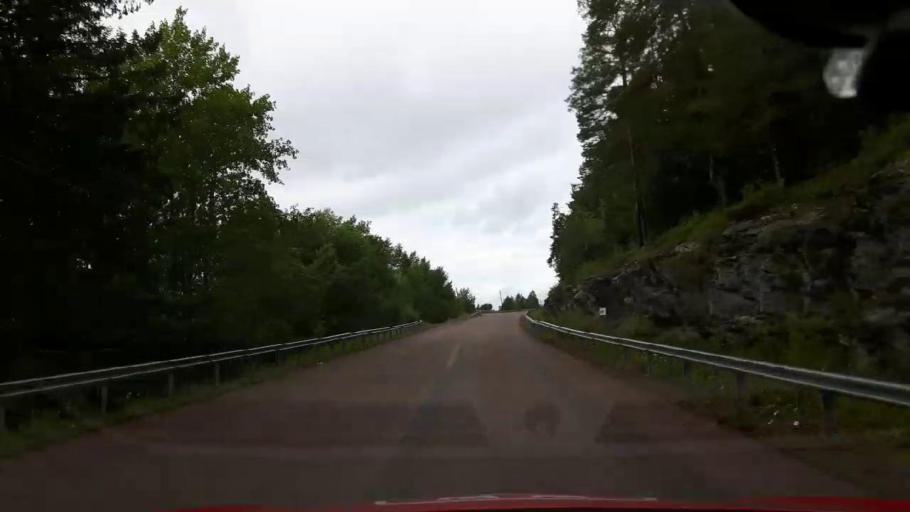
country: SE
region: Jaemtland
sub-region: Krokoms Kommun
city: Valla
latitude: 63.3573
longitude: 14.0804
